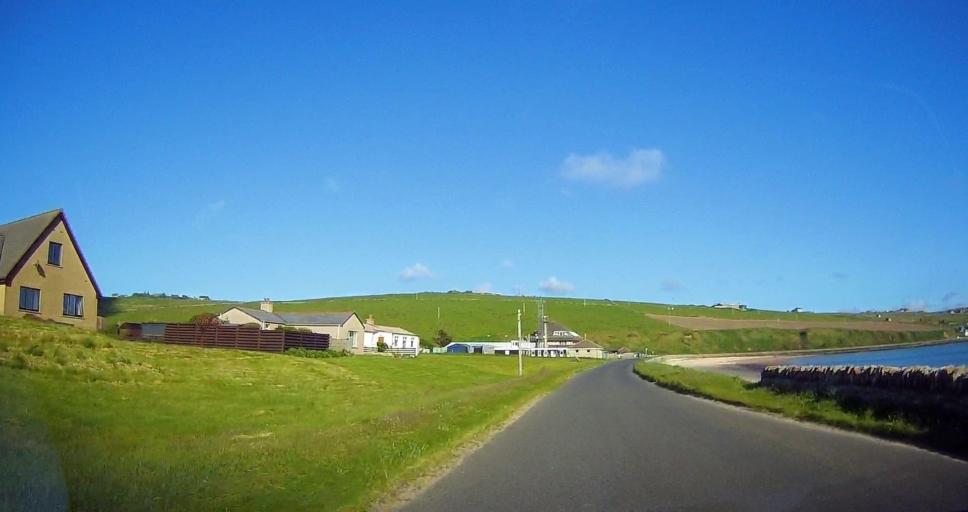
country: GB
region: Scotland
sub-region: Orkney Islands
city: Orkney
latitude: 58.9621
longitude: -2.9740
